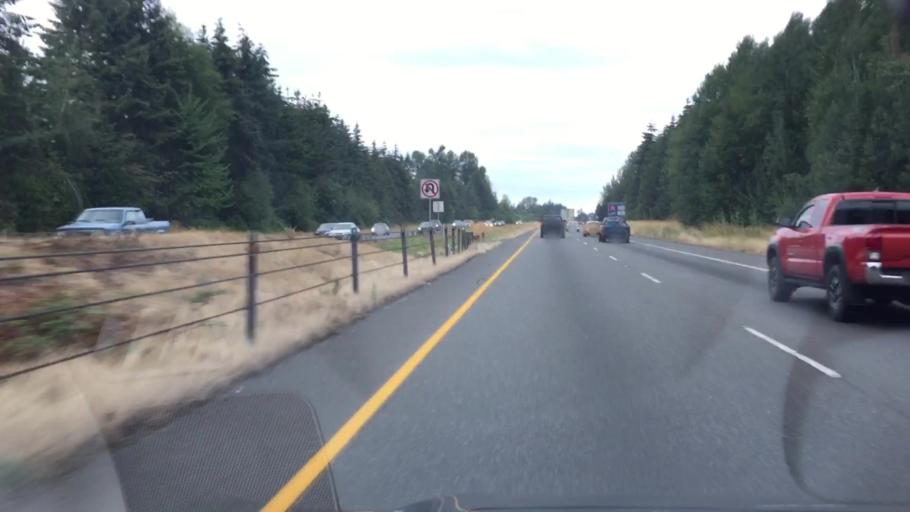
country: US
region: Washington
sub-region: Pierce County
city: Summit
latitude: 47.1584
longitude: -122.3786
